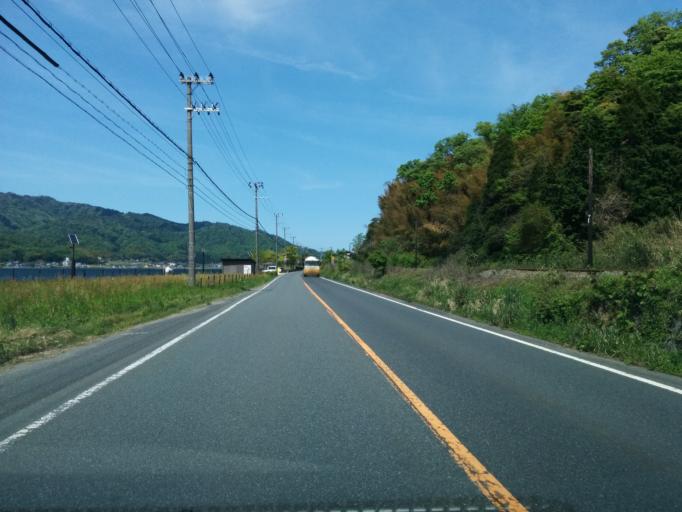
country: JP
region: Kyoto
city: Miyazu
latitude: 35.5605
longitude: 135.1679
